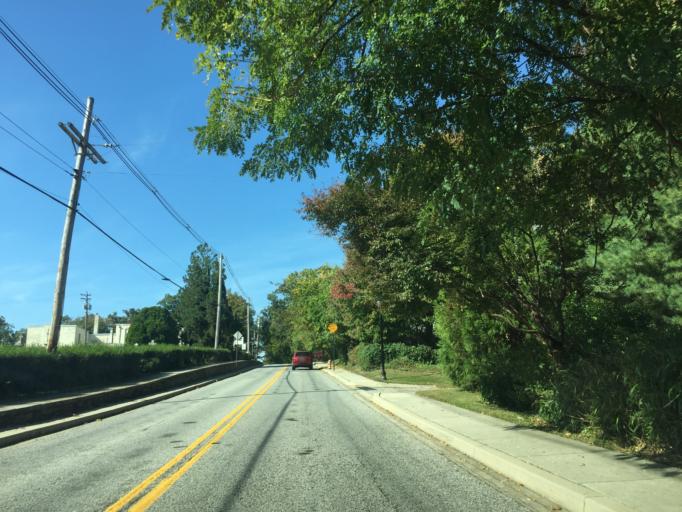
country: US
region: Maryland
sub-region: Baltimore County
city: Towson
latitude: 39.3537
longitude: -76.6165
